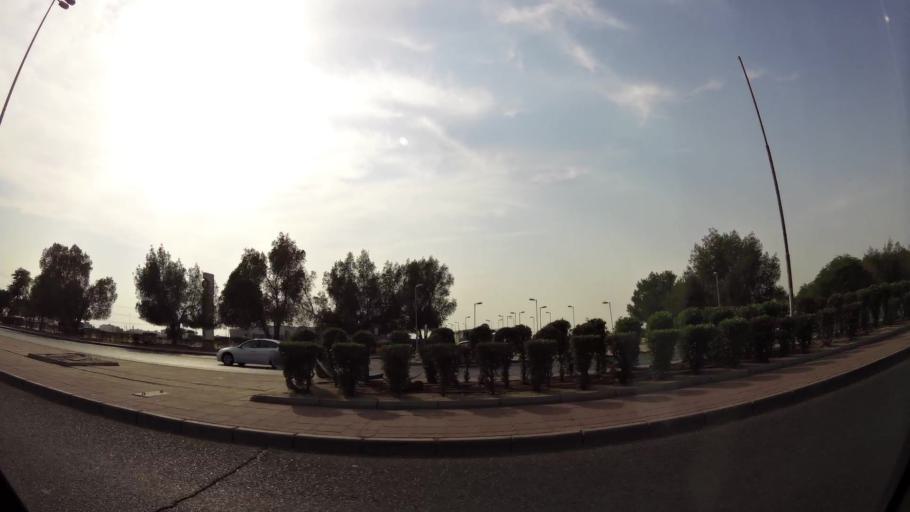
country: KW
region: Al Farwaniyah
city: Al Farwaniyah
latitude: 29.3076
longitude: 47.9627
